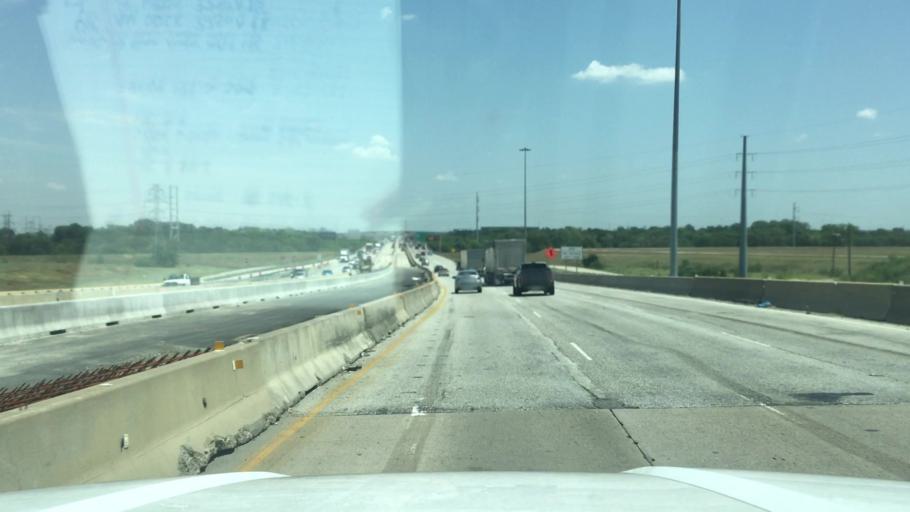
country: US
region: Texas
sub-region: Dallas County
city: Irving
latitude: 32.8479
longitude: -96.9099
